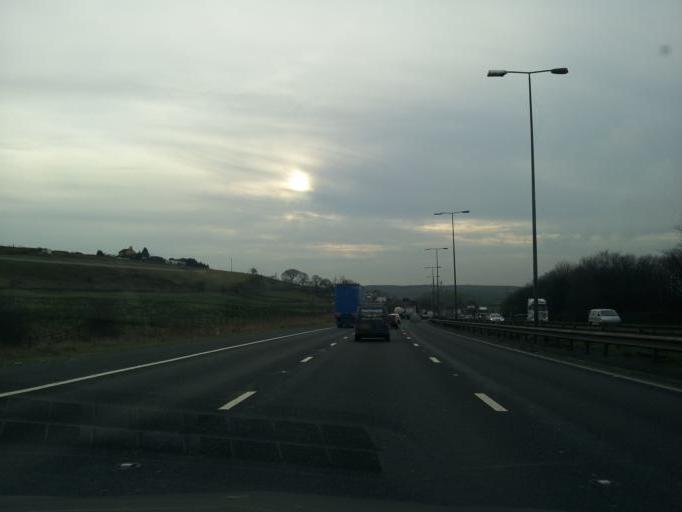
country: GB
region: England
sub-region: Borough of Rochdale
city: Milnrow
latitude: 53.6121
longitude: -2.0902
